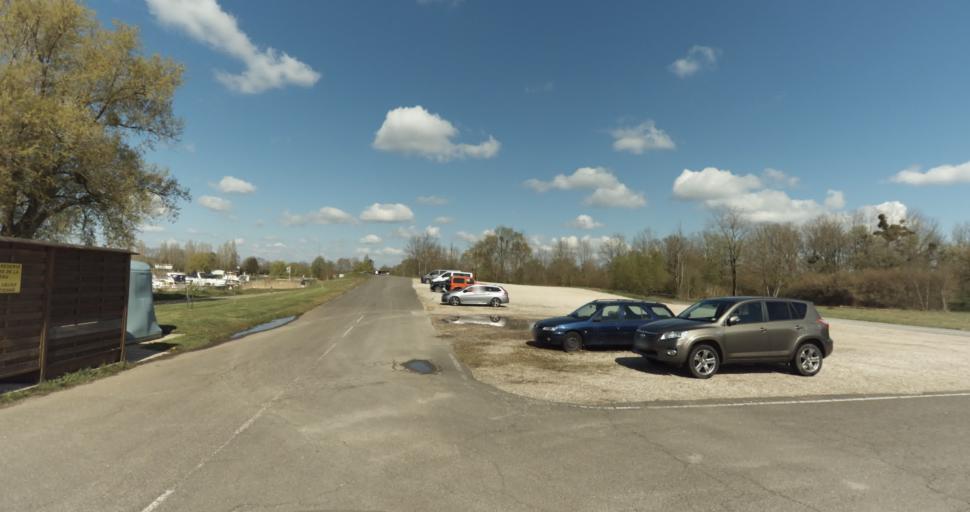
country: FR
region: Bourgogne
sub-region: Departement de la Cote-d'Or
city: Auxonne
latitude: 47.1985
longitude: 5.3891
